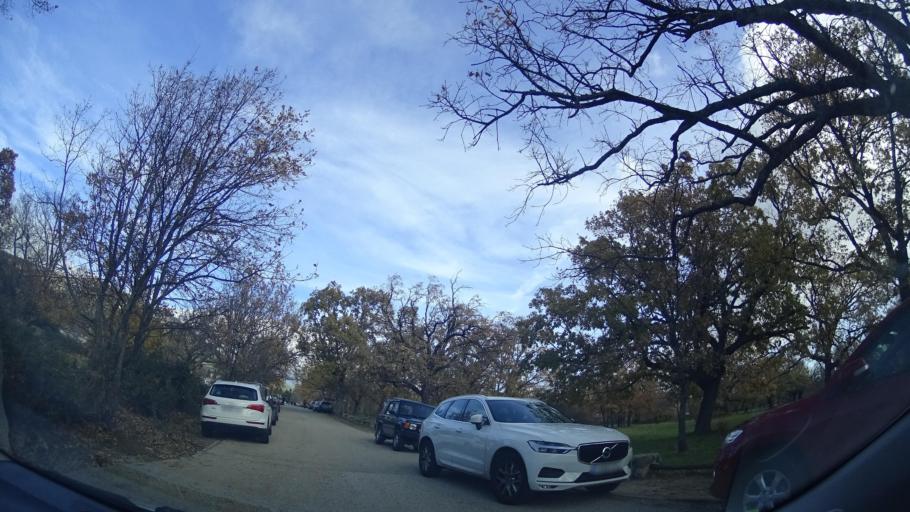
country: ES
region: Madrid
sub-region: Provincia de Madrid
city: San Lorenzo de El Escorial
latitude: 40.5830
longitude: -4.1450
